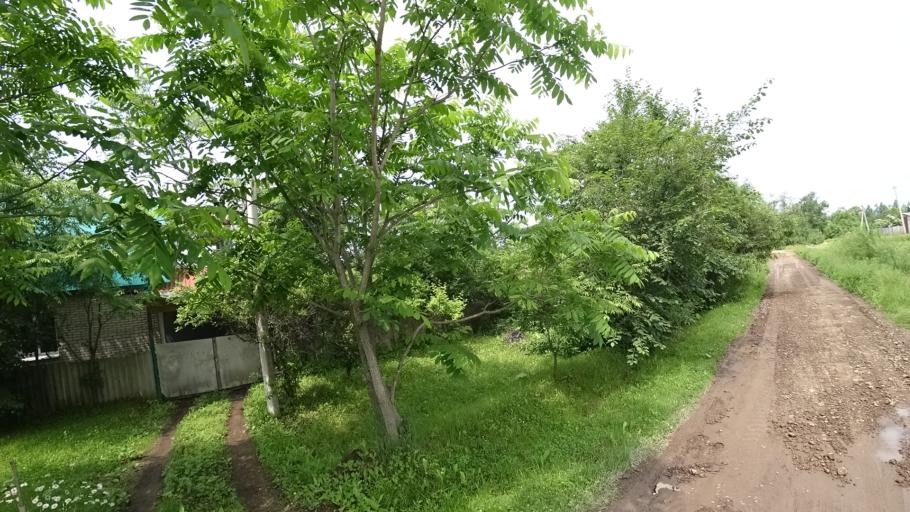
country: RU
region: Primorskiy
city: Novosysoyevka
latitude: 44.2457
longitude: 133.3792
